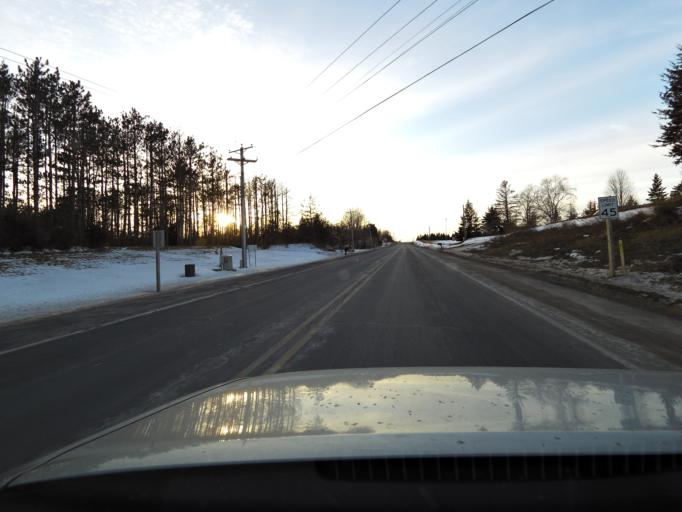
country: US
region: Wisconsin
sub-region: Saint Croix County
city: Hudson
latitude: 44.9779
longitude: -92.7147
